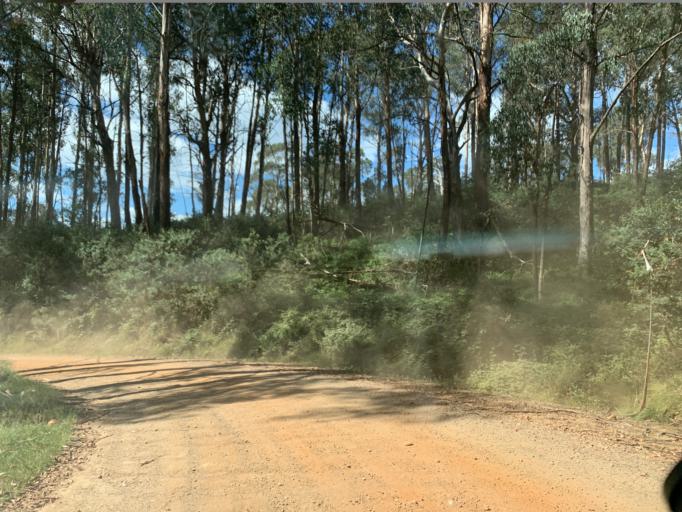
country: AU
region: Victoria
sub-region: Mansfield
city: Mansfield
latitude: -37.0948
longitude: 146.5412
